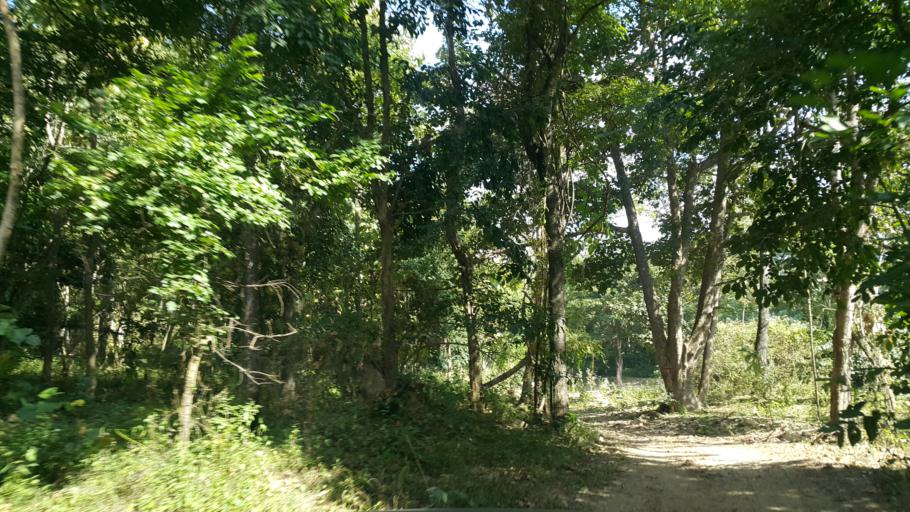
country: TH
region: Lamphun
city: Ban Thi
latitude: 18.5752
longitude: 99.1686
